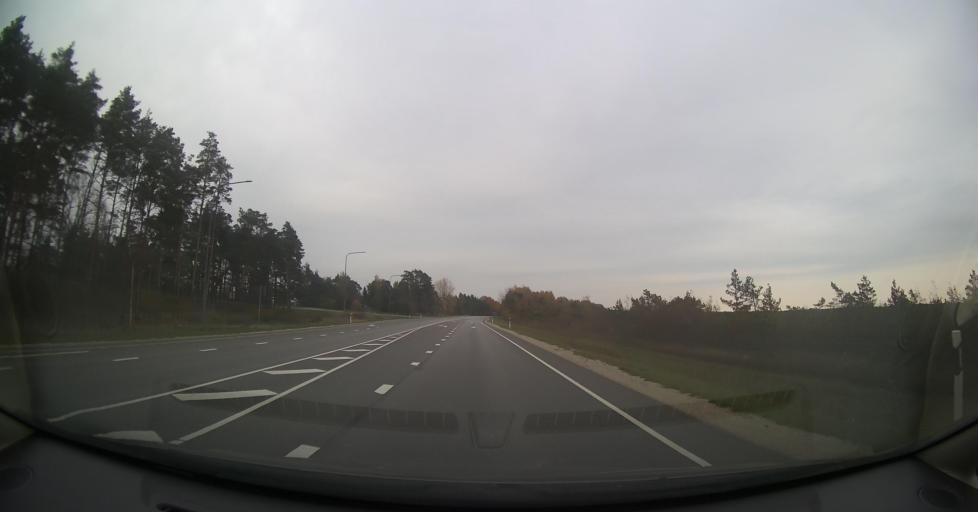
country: EE
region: Harju
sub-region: Nissi vald
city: Turba
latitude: 58.9934
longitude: 24.0706
